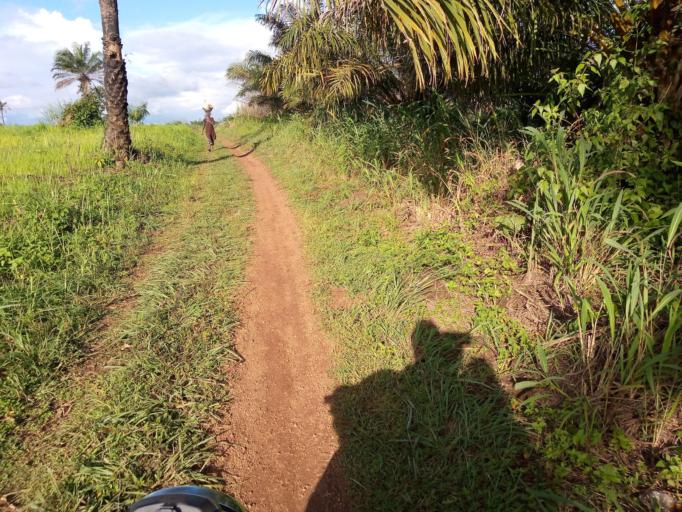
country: GN
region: Nzerekore
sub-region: Prefecture de Guekedou
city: Gueckedou
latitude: 8.4835
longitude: -10.3250
